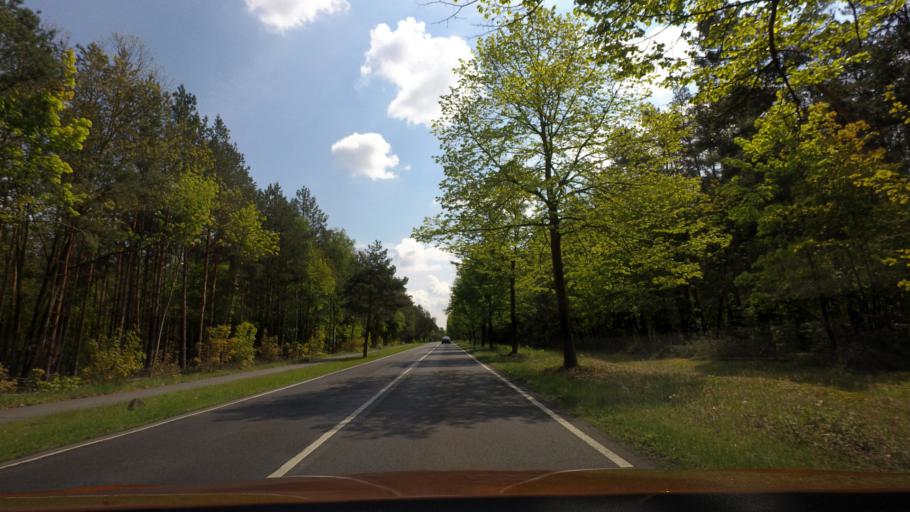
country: DE
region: Brandenburg
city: Zeuthen
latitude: 52.3973
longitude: 13.6081
